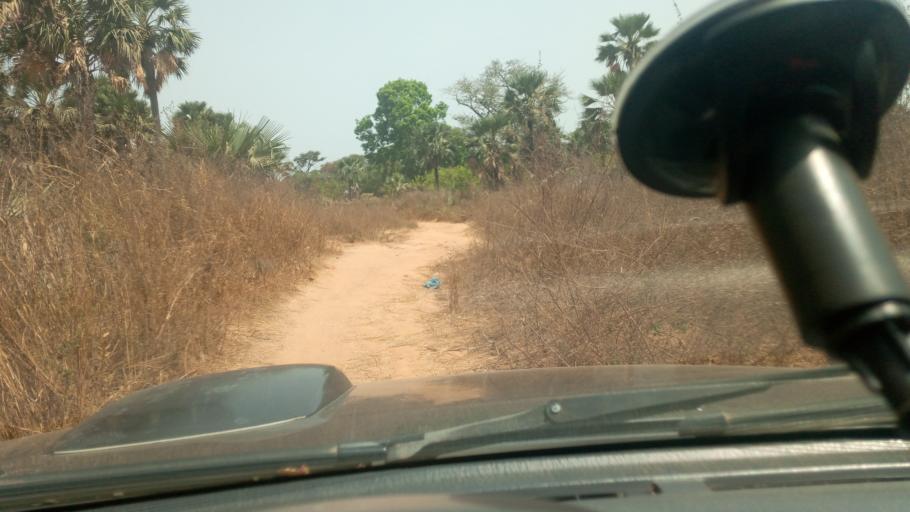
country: SN
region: Sedhiou
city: Sedhiou
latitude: 12.4465
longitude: -15.6160
